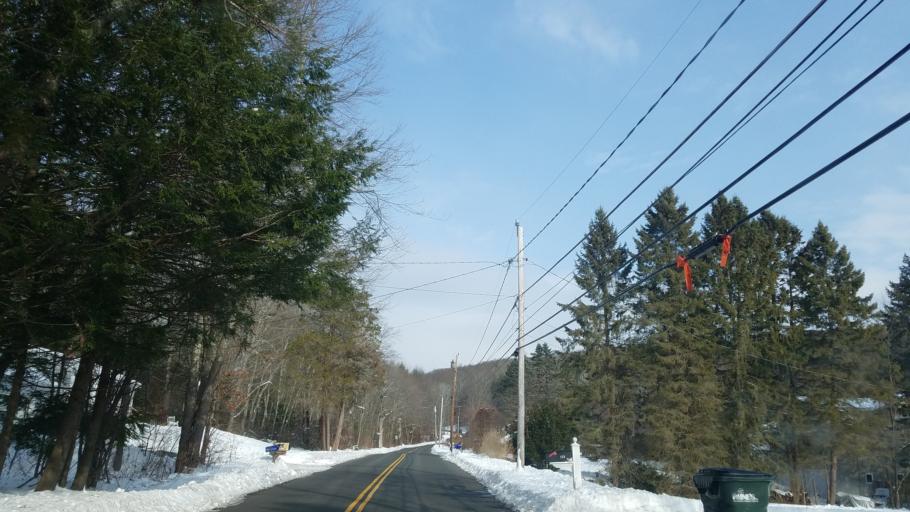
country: US
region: Connecticut
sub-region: Hartford County
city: Canton Valley
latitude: 41.8429
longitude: -72.9016
